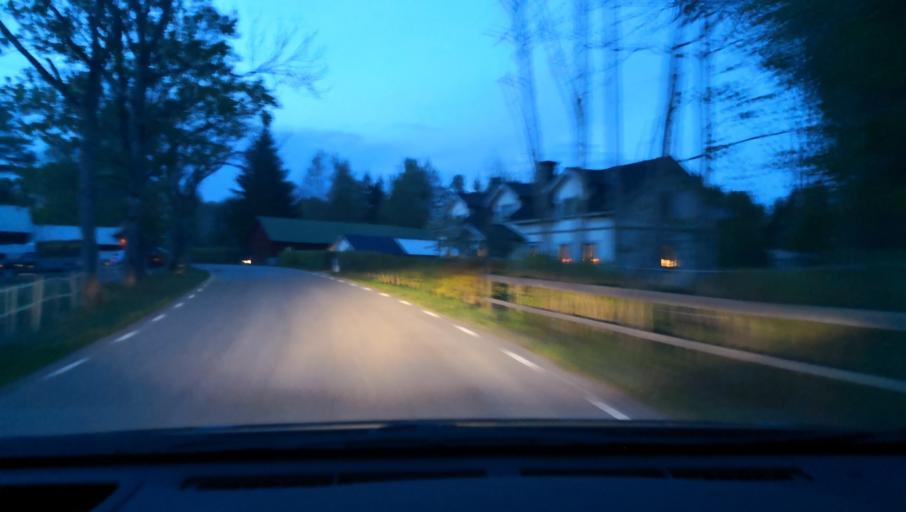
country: SE
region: OErebro
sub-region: Orebro Kommun
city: Vintrosa
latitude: 59.1737
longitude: 15.0162
